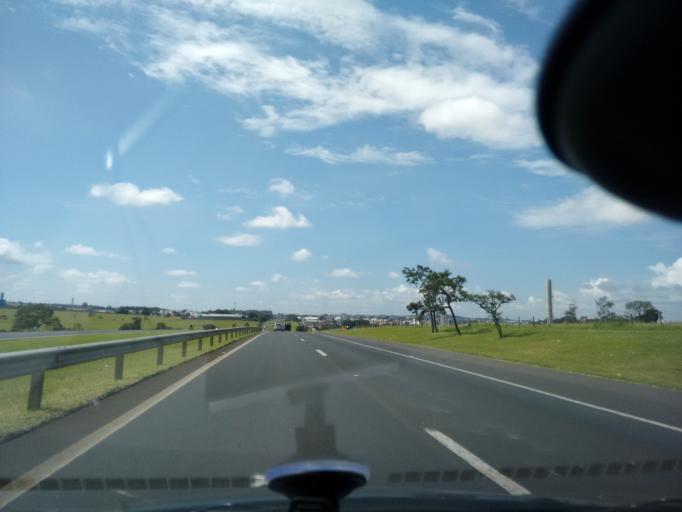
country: BR
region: Sao Paulo
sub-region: Sao Carlos
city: Sao Carlos
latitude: -21.9828
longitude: -47.9124
